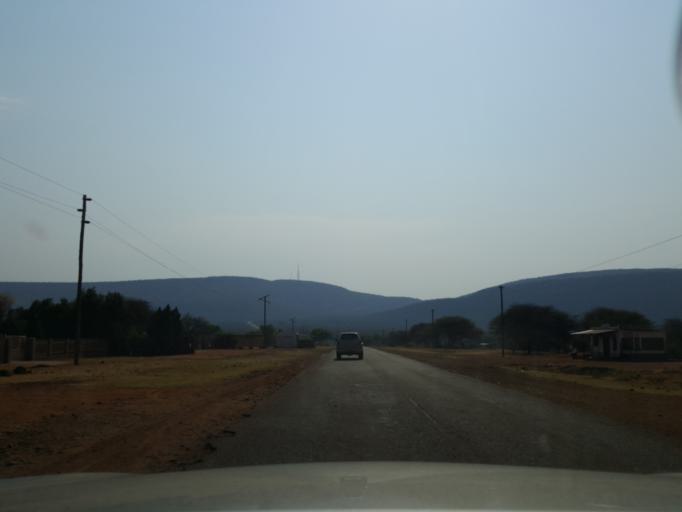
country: BW
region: South East
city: Lobatse
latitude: -25.2956
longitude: 25.8447
